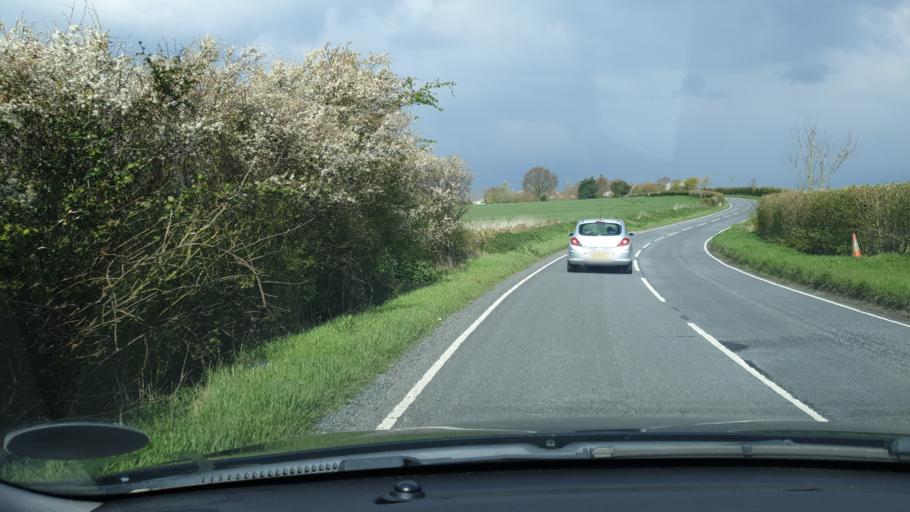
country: GB
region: England
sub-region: Essex
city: Mistley
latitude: 51.8975
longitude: 1.0914
